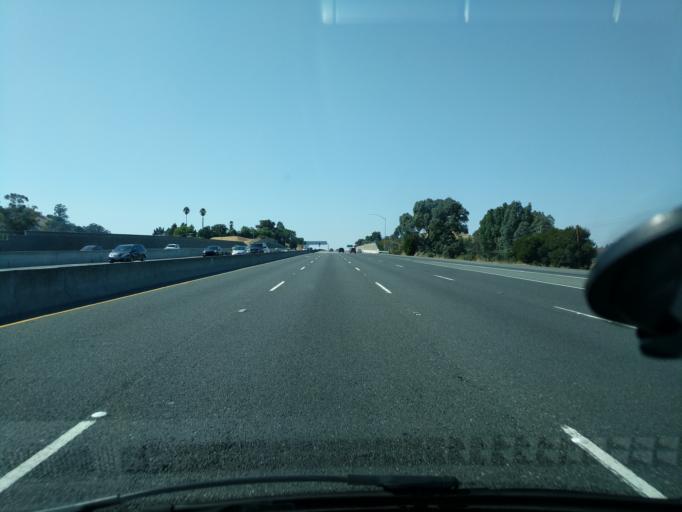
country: US
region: California
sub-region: Contra Costa County
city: Pacheco
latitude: 37.9970
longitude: -122.0728
